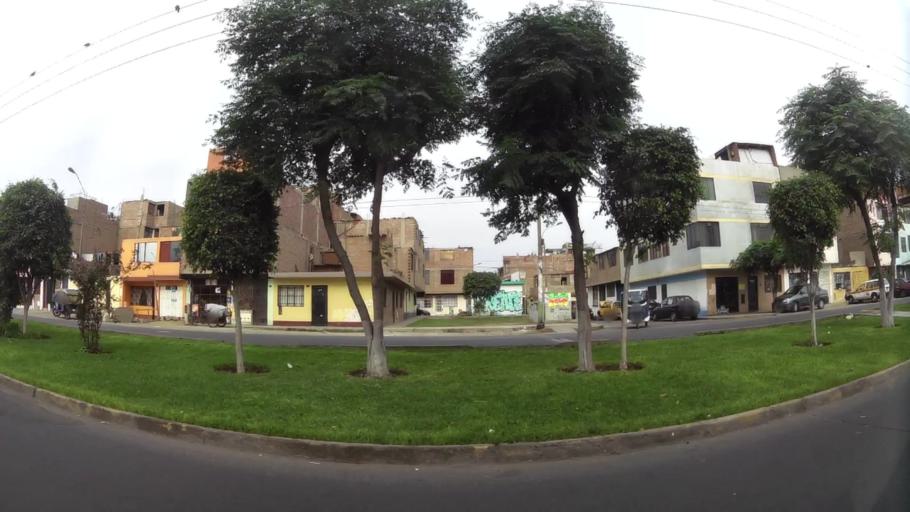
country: PE
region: Callao
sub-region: Callao
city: Callao
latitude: -12.0221
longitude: -77.0976
